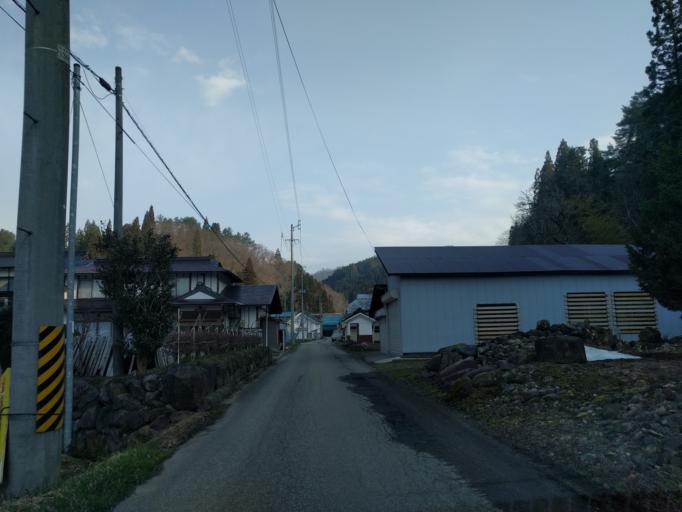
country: JP
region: Fukushima
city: Kitakata
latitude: 37.7043
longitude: 139.9120
